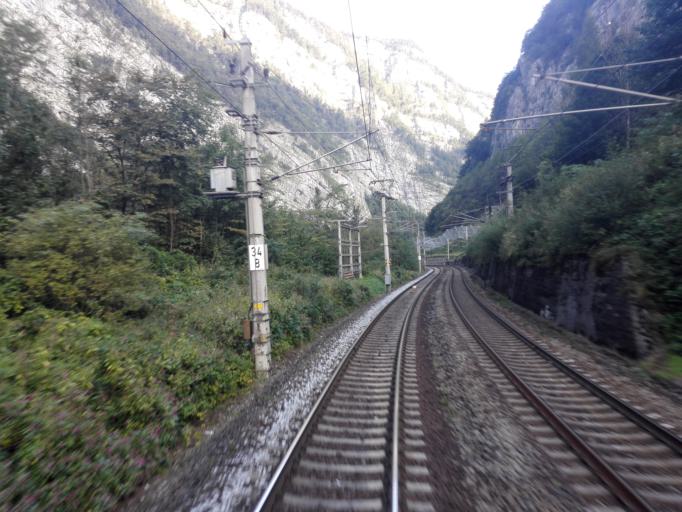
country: AT
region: Salzburg
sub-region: Politischer Bezirk Hallein
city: Golling an der Salzach
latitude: 47.5624
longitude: 13.1673
